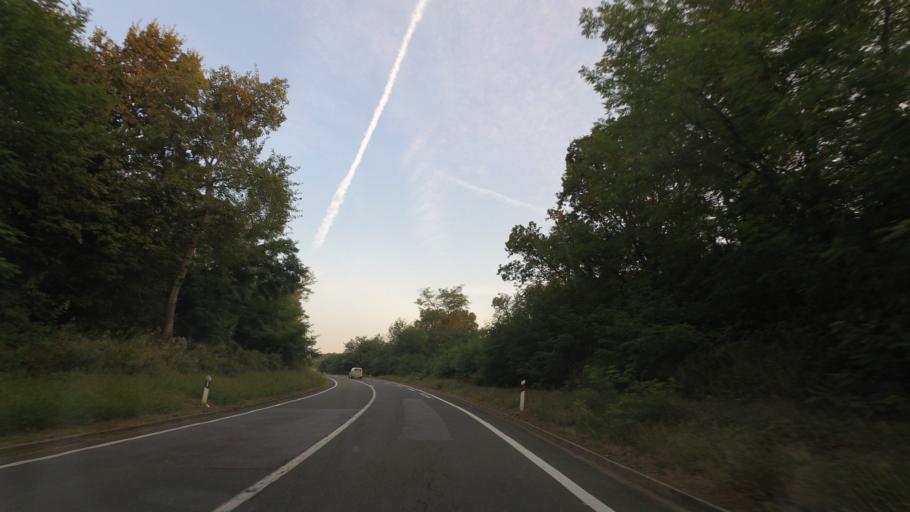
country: HR
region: Brodsko-Posavska
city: Nova Gradiska
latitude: 45.2664
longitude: 17.4098
